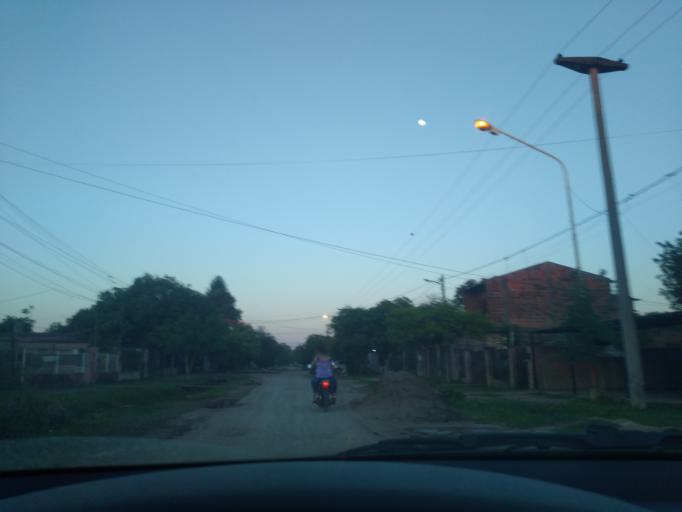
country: AR
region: Chaco
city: Barranqueras
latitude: -27.4756
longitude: -58.9332
